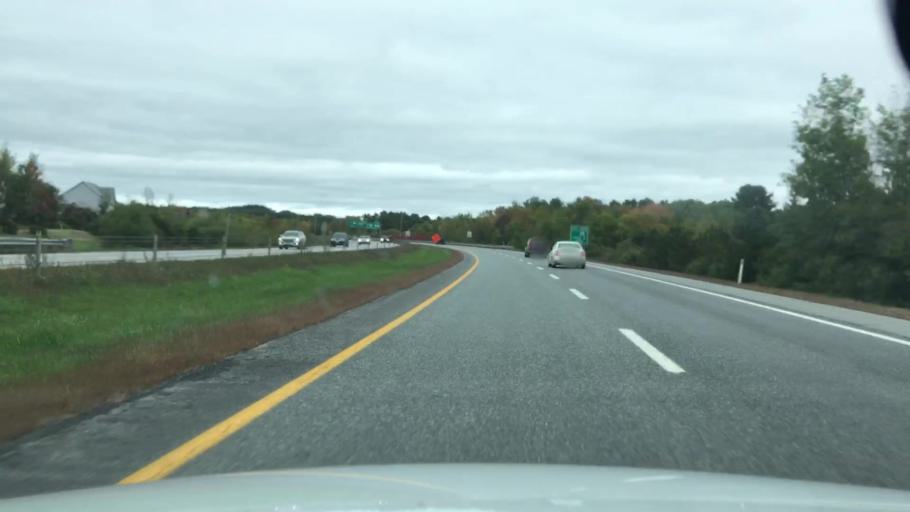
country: US
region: Maine
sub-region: Penobscot County
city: Hampden
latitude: 44.7811
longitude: -68.8158
